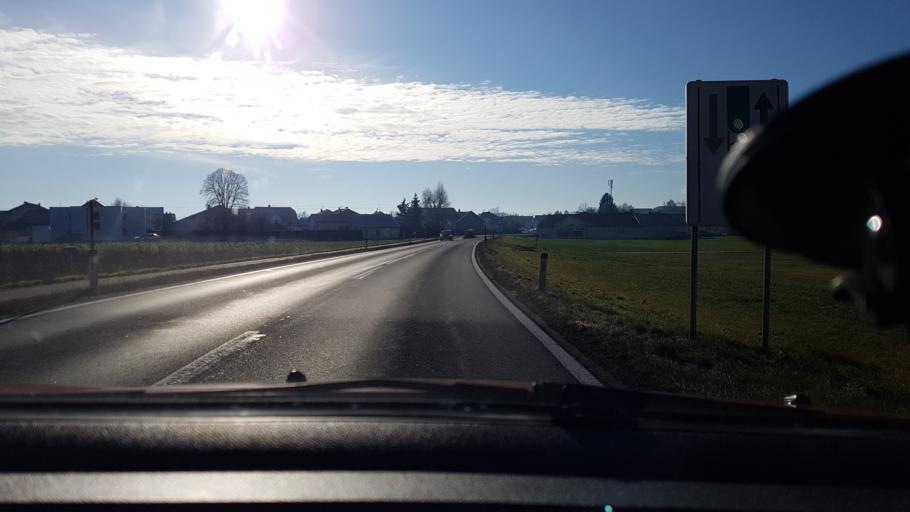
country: AT
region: Upper Austria
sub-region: Politischer Bezirk Braunau am Inn
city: Braunau am Inn
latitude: 48.1823
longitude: 13.0545
